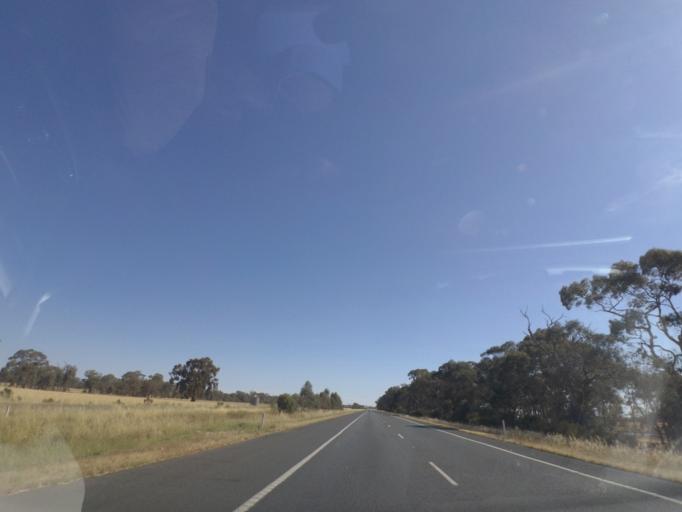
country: AU
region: Victoria
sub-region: Greater Shepparton
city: Shepparton
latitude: -36.7392
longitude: 145.1851
